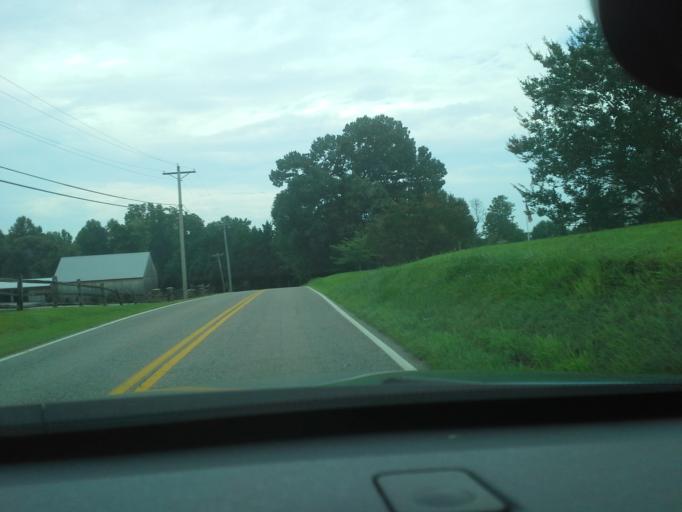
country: US
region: Maryland
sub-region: Calvert County
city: Dunkirk Town Center
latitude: 38.7335
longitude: -76.6437
